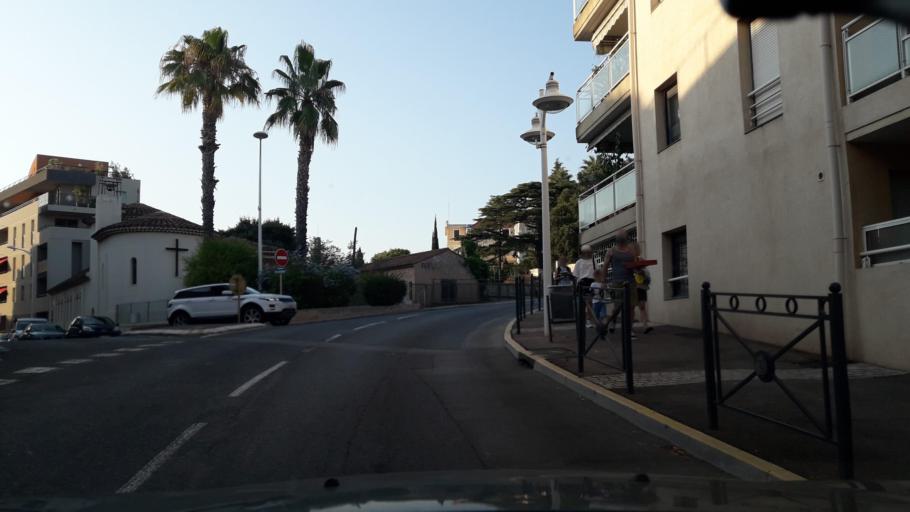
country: FR
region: Provence-Alpes-Cote d'Azur
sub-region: Departement du Var
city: Saint-Raphael
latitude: 43.4206
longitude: 6.7715
